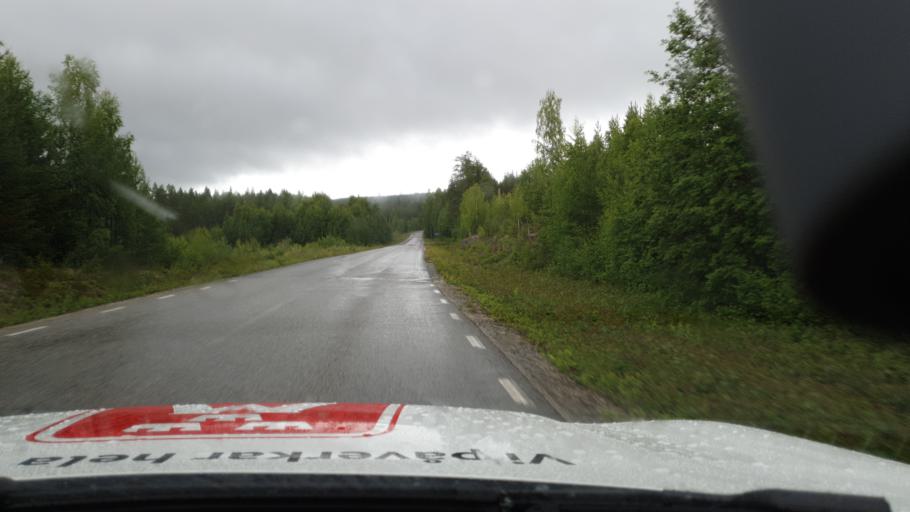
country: SE
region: Vaesterbotten
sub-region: Vindelns Kommun
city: Vindeln
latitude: 64.3229
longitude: 19.6213
